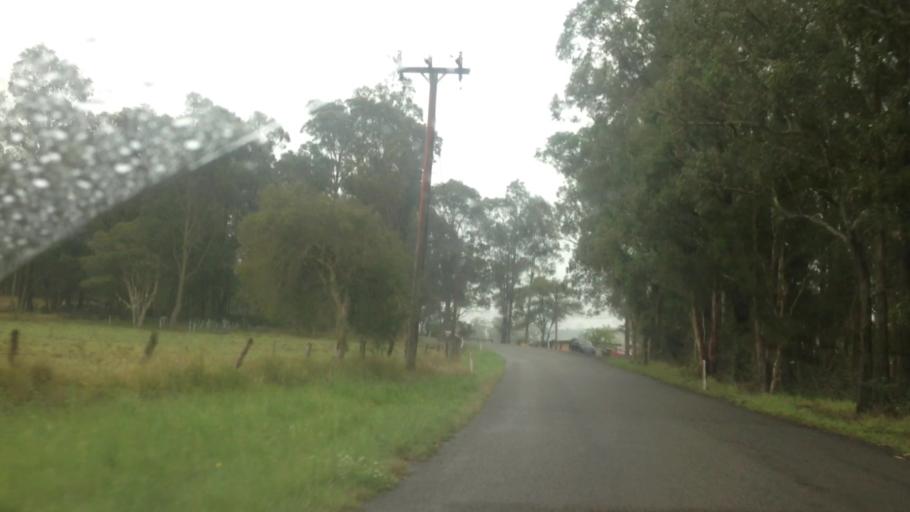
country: AU
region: New South Wales
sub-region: Wyong Shire
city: Little Jilliby
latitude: -33.2151
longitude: 151.3717
